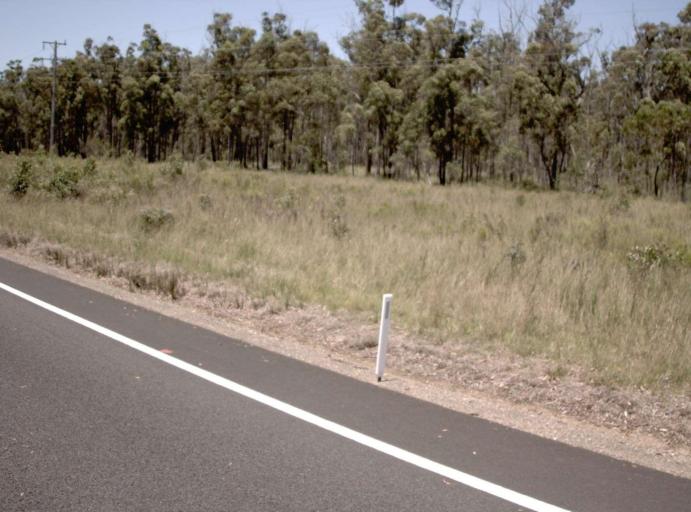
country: AU
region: Victoria
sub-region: East Gippsland
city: Lakes Entrance
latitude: -37.7551
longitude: 148.3111
